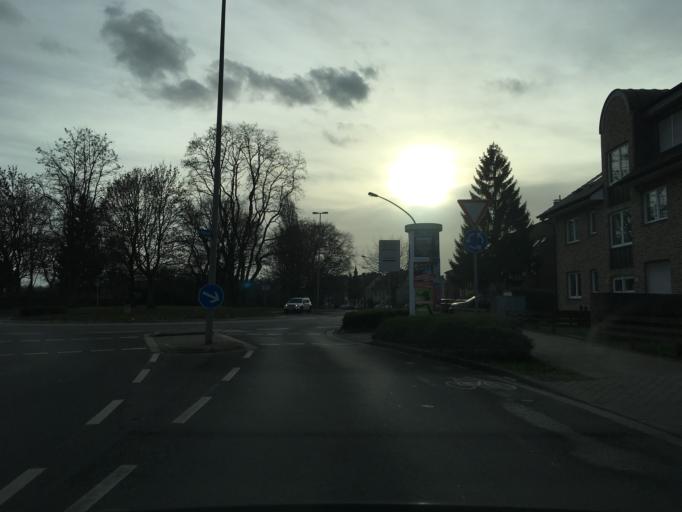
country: DE
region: North Rhine-Westphalia
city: Meiderich
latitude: 51.5206
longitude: 6.7870
